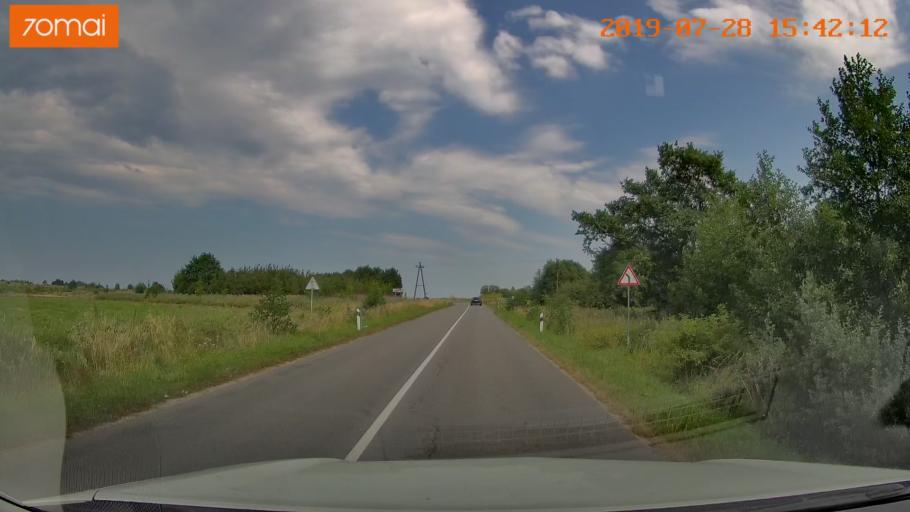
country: RU
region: Kaliningrad
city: Donskoye
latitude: 54.9298
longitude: 20.0070
